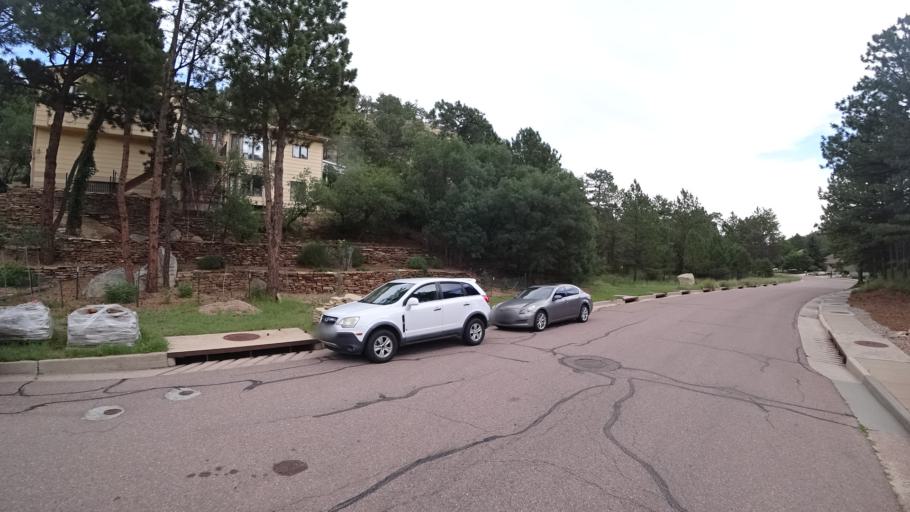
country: US
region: Colorado
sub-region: El Paso County
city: Colorado Springs
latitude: 38.9084
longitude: -104.8391
